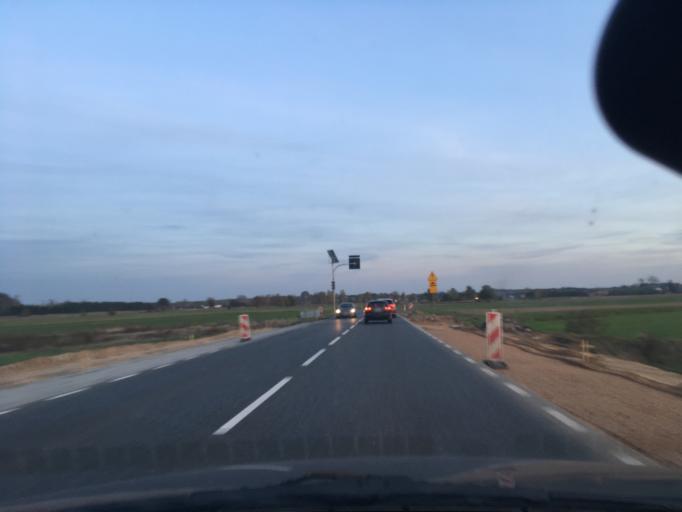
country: PL
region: Masovian Voivodeship
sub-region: Powiat plocki
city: Wyszogrod
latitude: 52.3613
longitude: 20.1999
